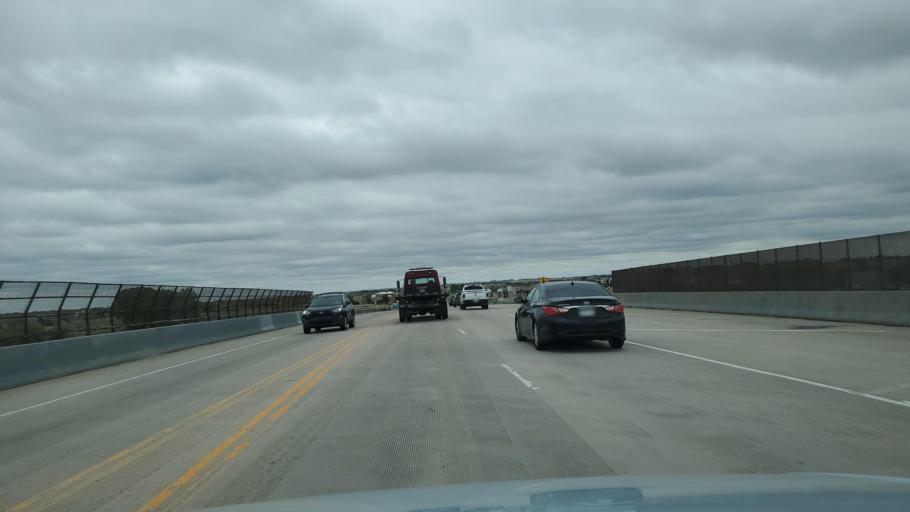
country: US
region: Colorado
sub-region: Adams County
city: Brighton
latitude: 39.9143
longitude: -104.8143
